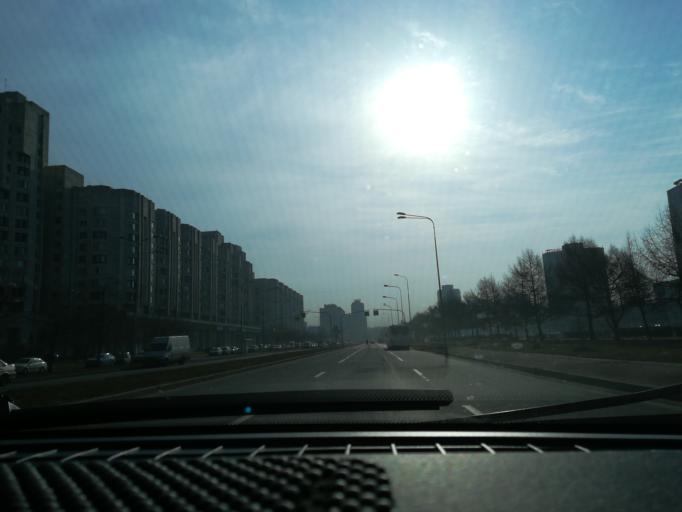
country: RU
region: St.-Petersburg
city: Vasyl'evsky Ostrov
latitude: 59.9497
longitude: 30.2228
